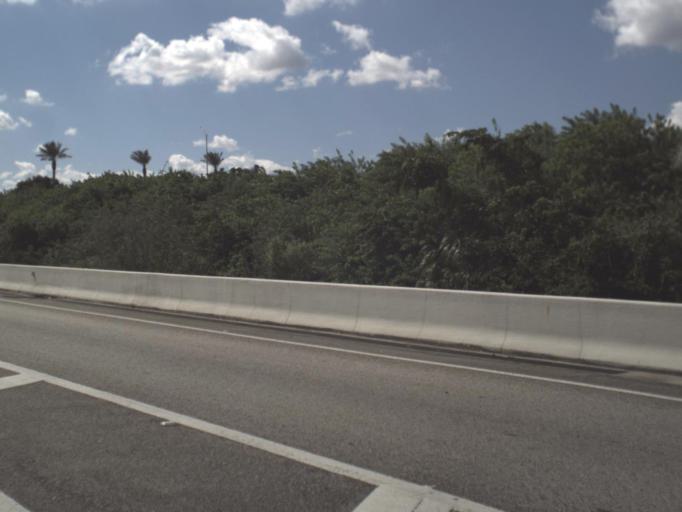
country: US
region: Florida
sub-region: Broward County
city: Palm Aire
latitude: 26.1933
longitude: -80.2100
